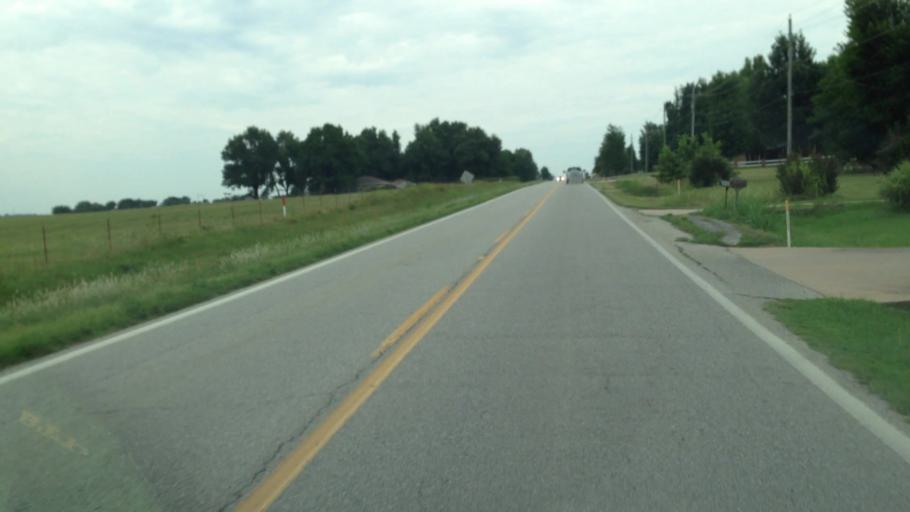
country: US
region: Oklahoma
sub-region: Craig County
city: Vinita
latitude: 36.6639
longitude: -95.1436
